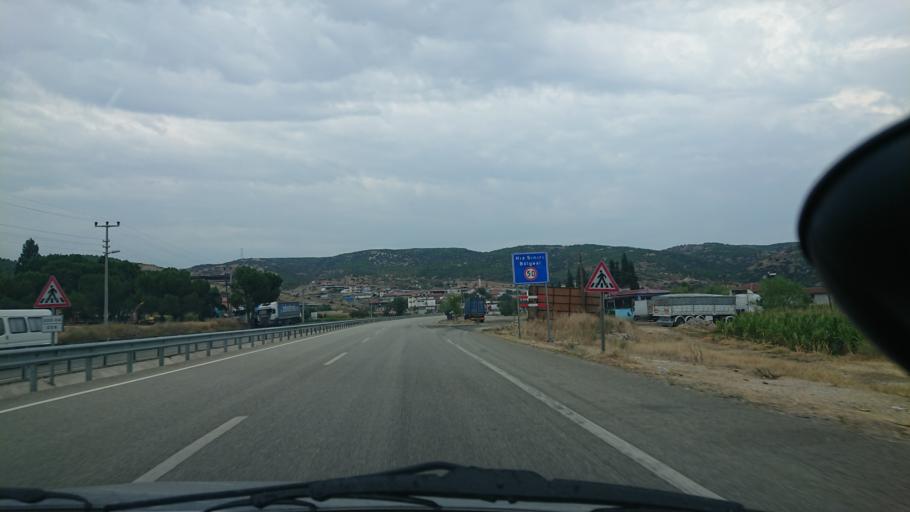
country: TR
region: Manisa
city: Selendi
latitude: 38.5959
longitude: 28.8125
